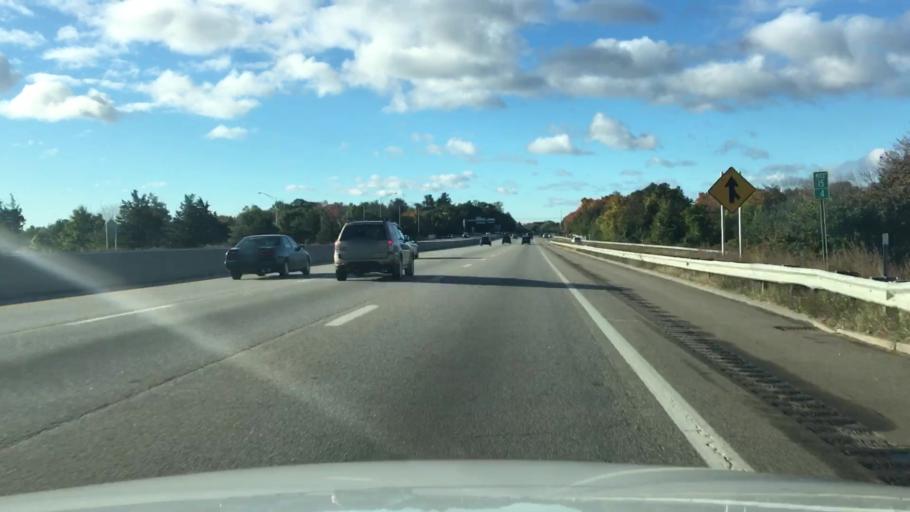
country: US
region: New Hampshire
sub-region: Rockingham County
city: Portsmouth
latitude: 43.0839
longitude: -70.7738
